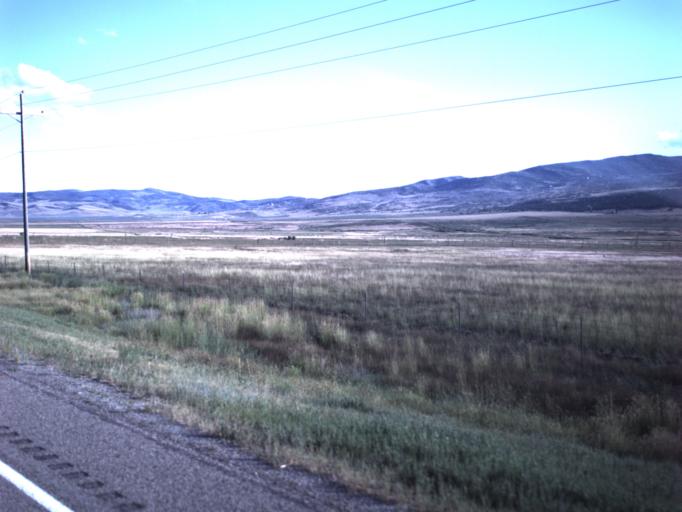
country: US
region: Utah
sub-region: Sanpete County
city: Fairview
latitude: 39.8031
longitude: -111.5024
